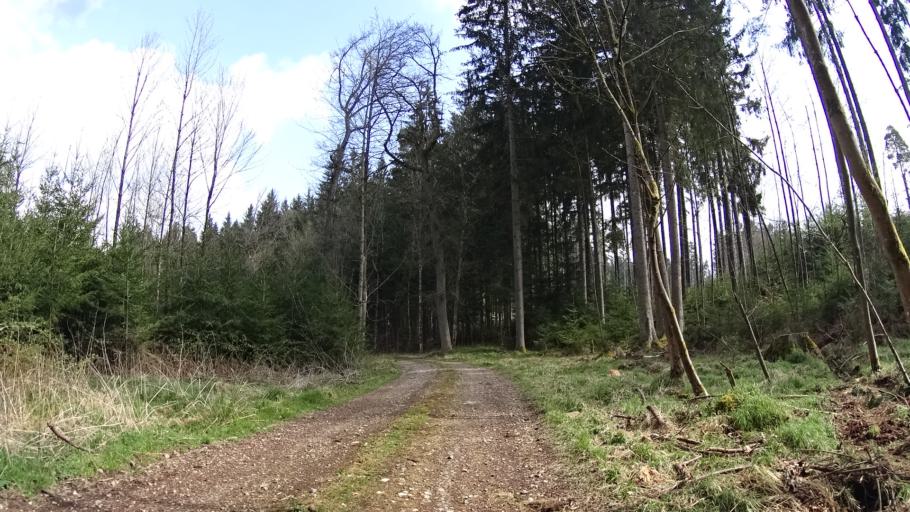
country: DE
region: Bavaria
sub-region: Upper Bavaria
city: Bohmfeld
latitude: 48.8734
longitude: 11.4051
